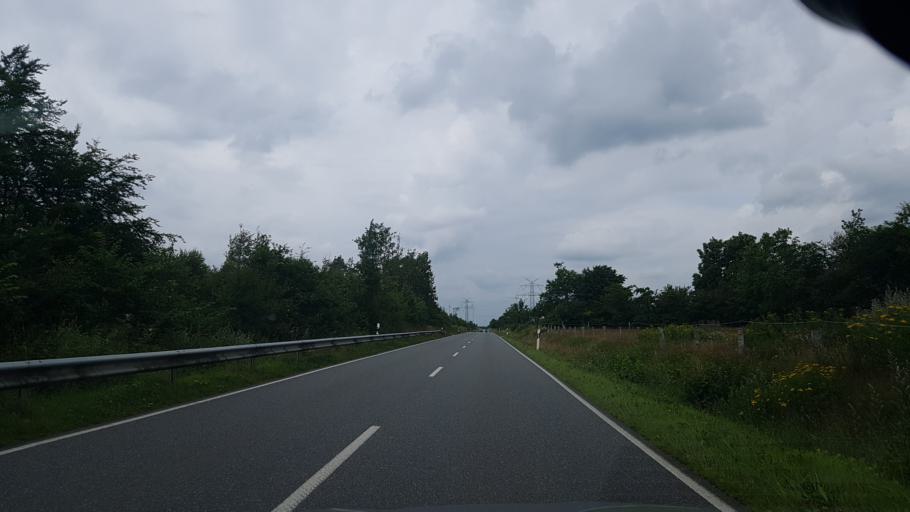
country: DE
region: Schleswig-Holstein
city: Jardelund
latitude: 54.8237
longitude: 9.2207
